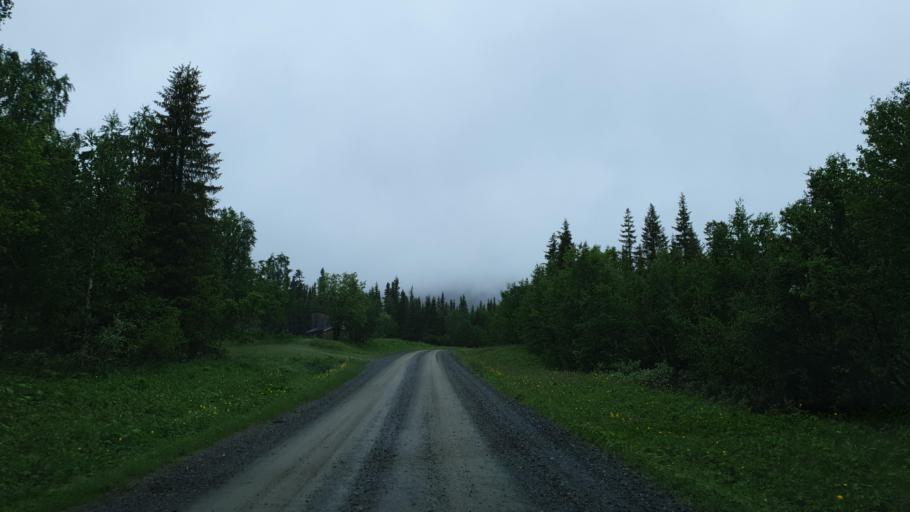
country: SE
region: Vaesterbotten
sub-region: Vilhelmina Kommun
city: Sjoberg
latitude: 65.2770
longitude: 15.8976
